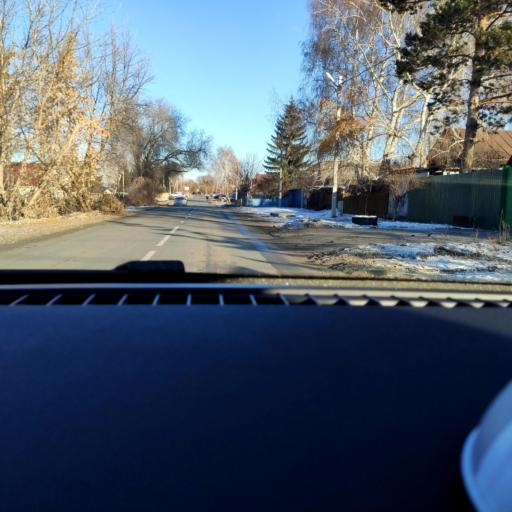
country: RU
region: Samara
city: Novokuybyshevsk
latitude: 53.1186
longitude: 49.8923
